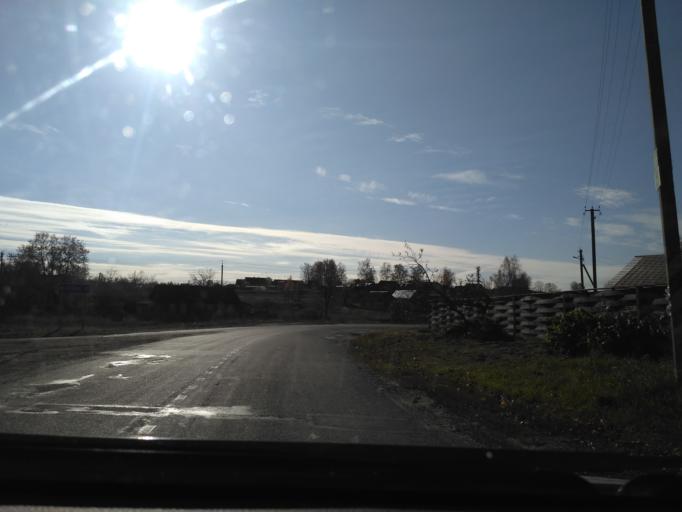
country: BY
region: Minsk
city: Loshnitsa
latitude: 54.3623
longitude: 28.6252
